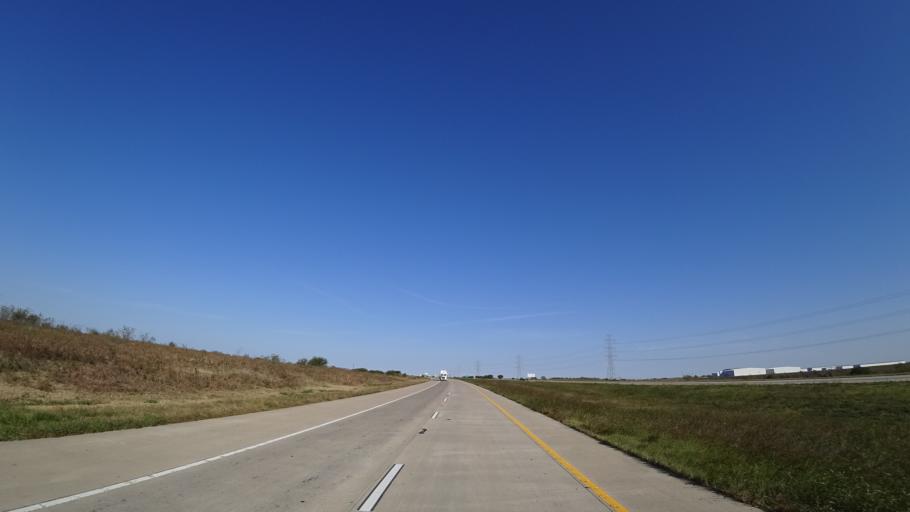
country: US
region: Texas
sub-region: Travis County
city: Manor
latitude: 30.3918
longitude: -97.5792
